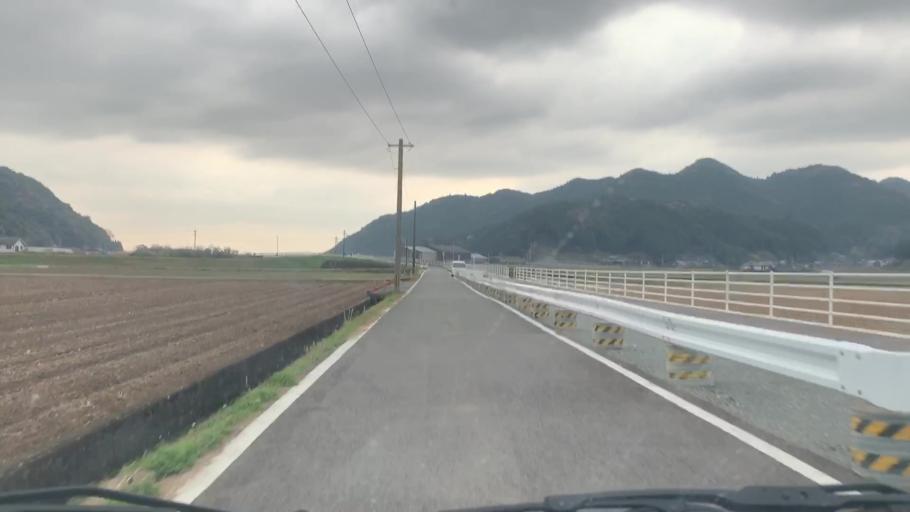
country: JP
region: Saga Prefecture
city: Ureshinomachi-shimojuku
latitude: 33.1267
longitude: 130.0331
